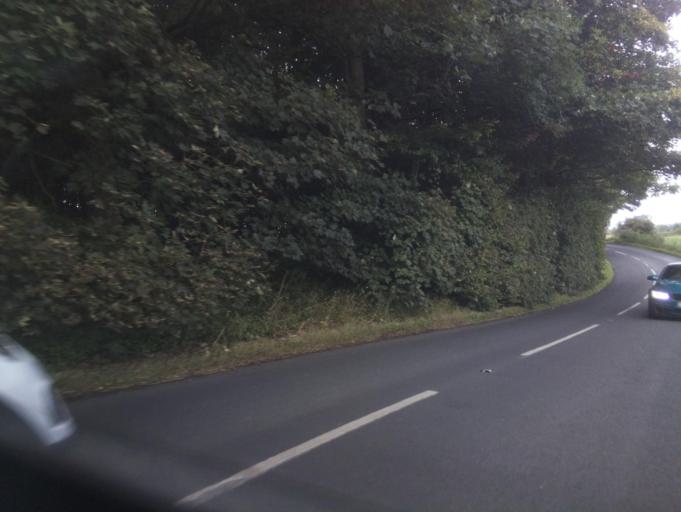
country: GB
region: England
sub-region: North Yorkshire
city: Catterick Garrison
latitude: 54.2567
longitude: -1.7160
